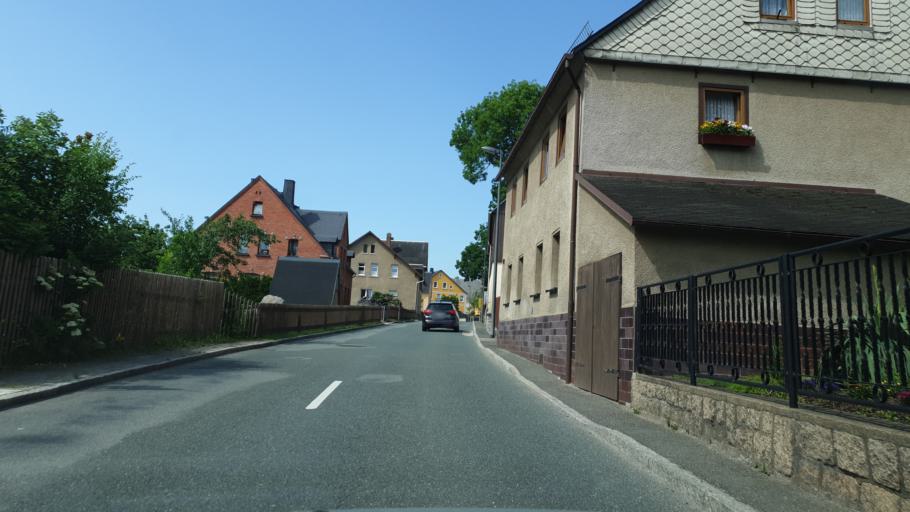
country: DE
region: Saxony
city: Zschorlau
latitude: 50.5639
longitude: 12.6432
